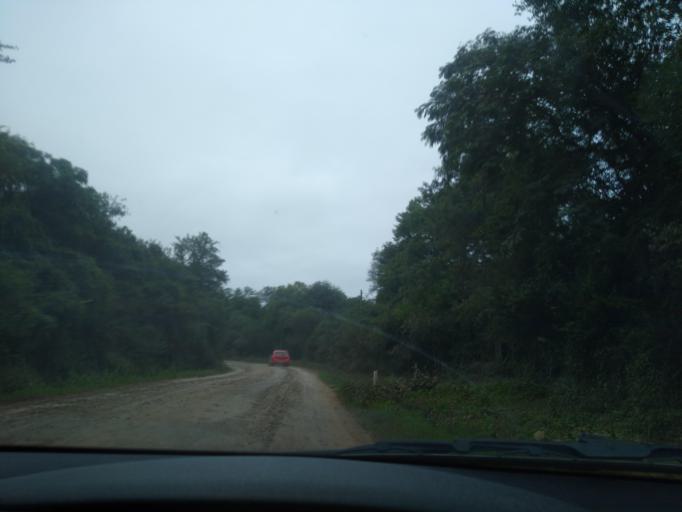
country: AR
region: Chaco
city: Colonia Benitez
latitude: -27.3384
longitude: -58.9684
